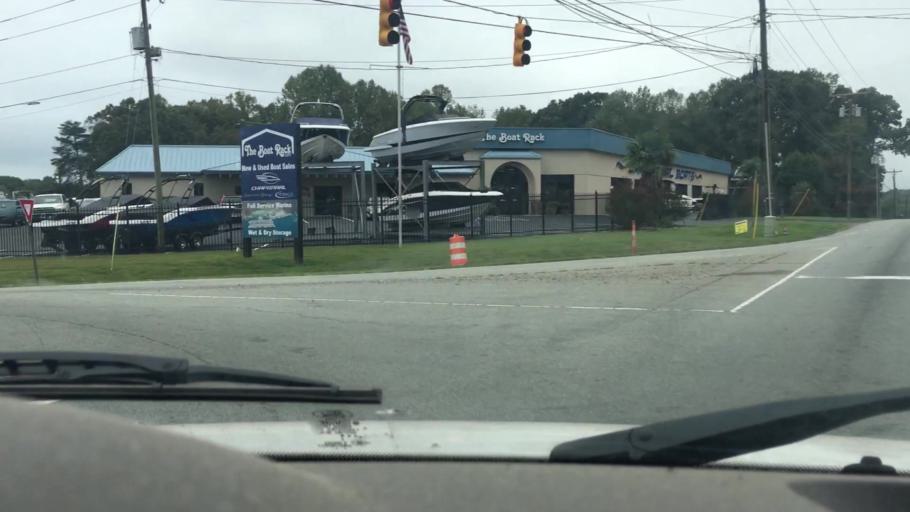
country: US
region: North Carolina
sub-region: Catawba County
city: Lake Norman of Catawba
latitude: 35.5823
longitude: -80.9914
